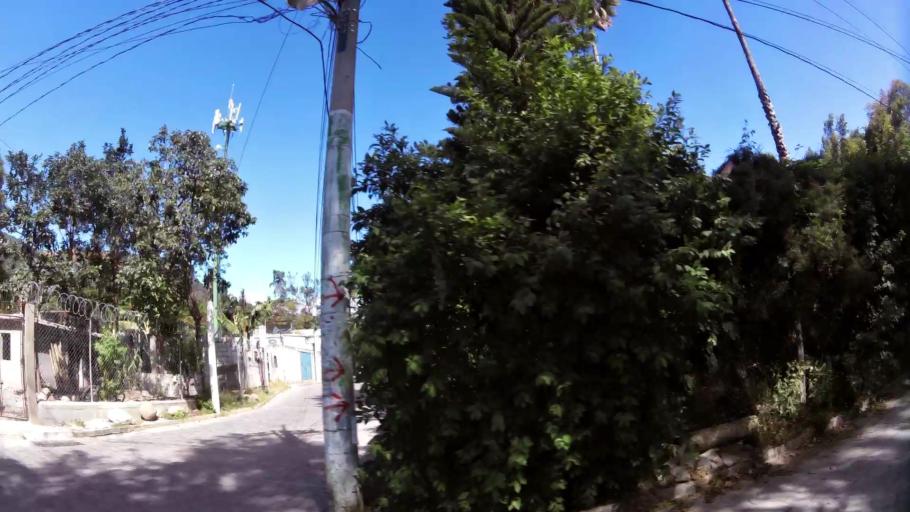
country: GT
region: Solola
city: Panajachel
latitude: 14.7401
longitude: -91.1552
